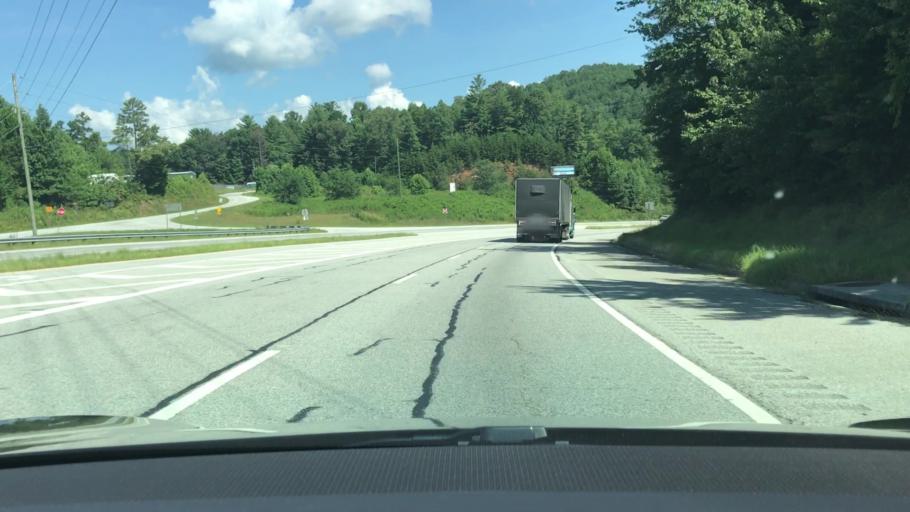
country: US
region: Georgia
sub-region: Rabun County
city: Clayton
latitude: 34.8294
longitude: -83.4262
